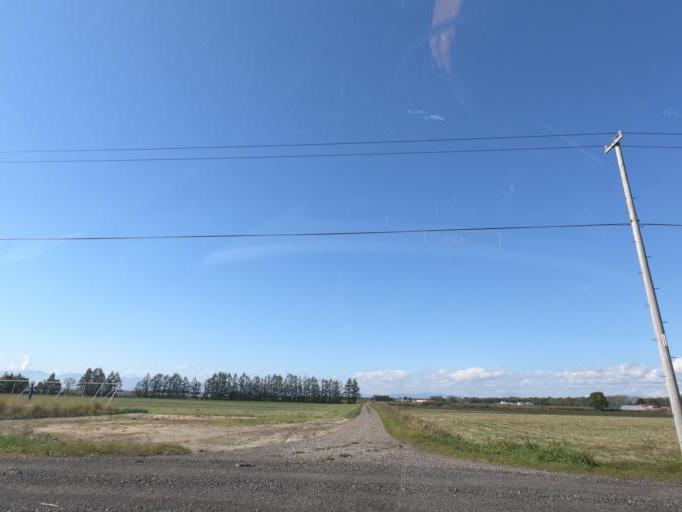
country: JP
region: Hokkaido
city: Otofuke
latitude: 43.0717
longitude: 143.2589
